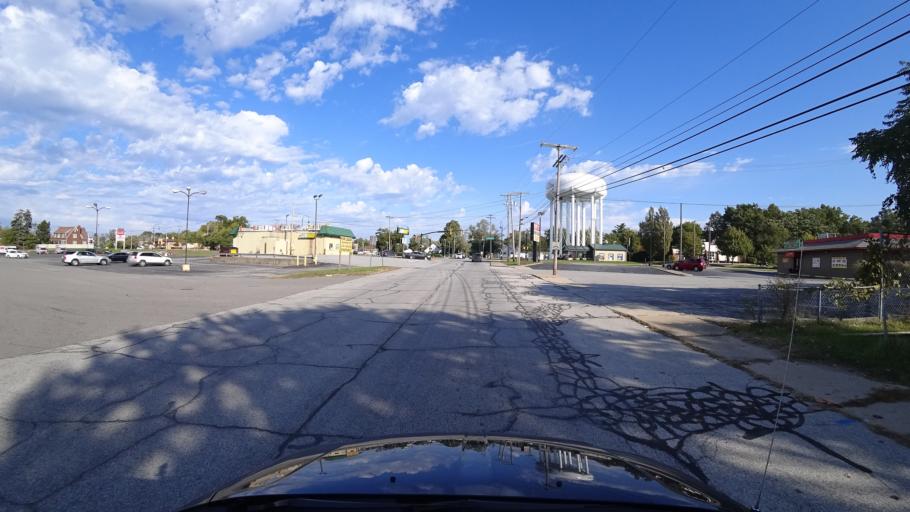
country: US
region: Indiana
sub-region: LaPorte County
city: Trail Creek
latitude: 41.7078
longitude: -86.8697
